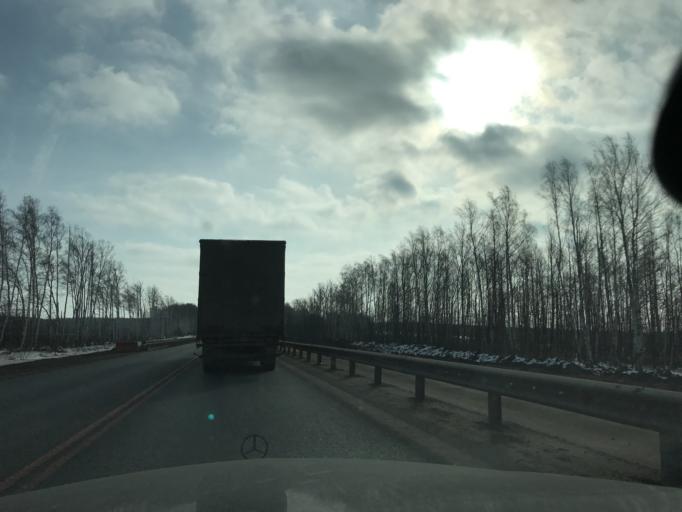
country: RU
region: Vladimir
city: Novovyazniki
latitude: 56.2120
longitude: 42.2634
